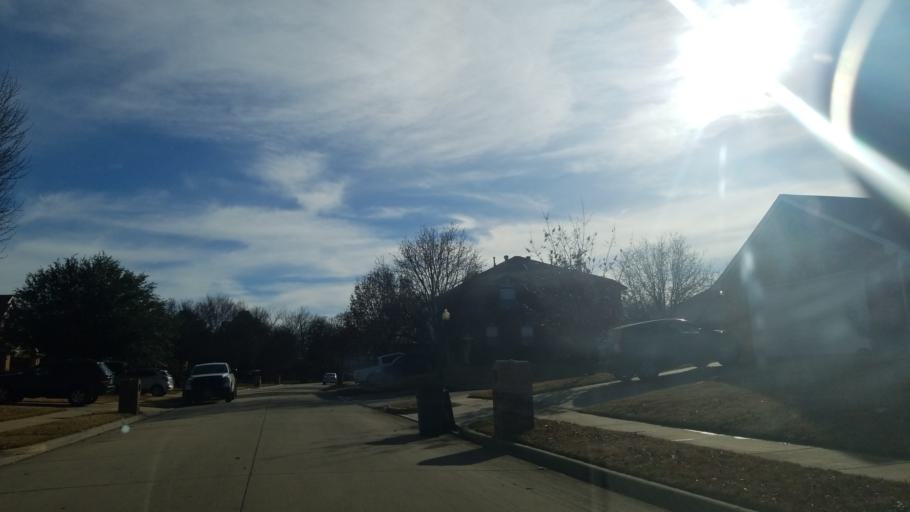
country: US
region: Texas
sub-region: Denton County
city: Corinth
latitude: 33.1409
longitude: -97.0638
